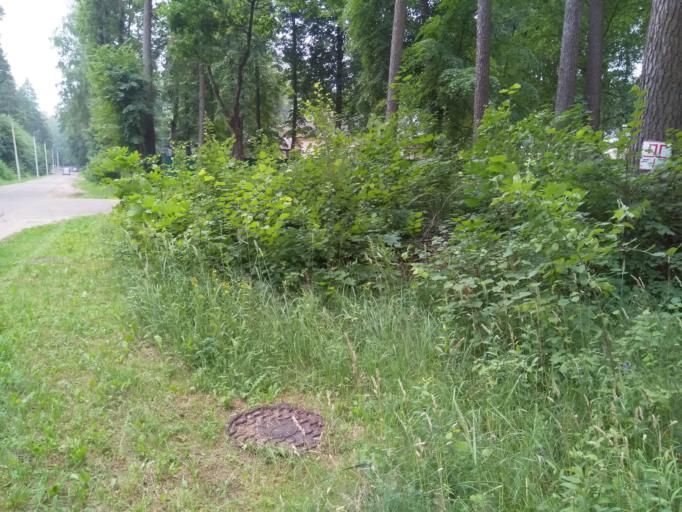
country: BY
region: Mogilev
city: Myazhysyatki
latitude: 53.8555
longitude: 30.1628
